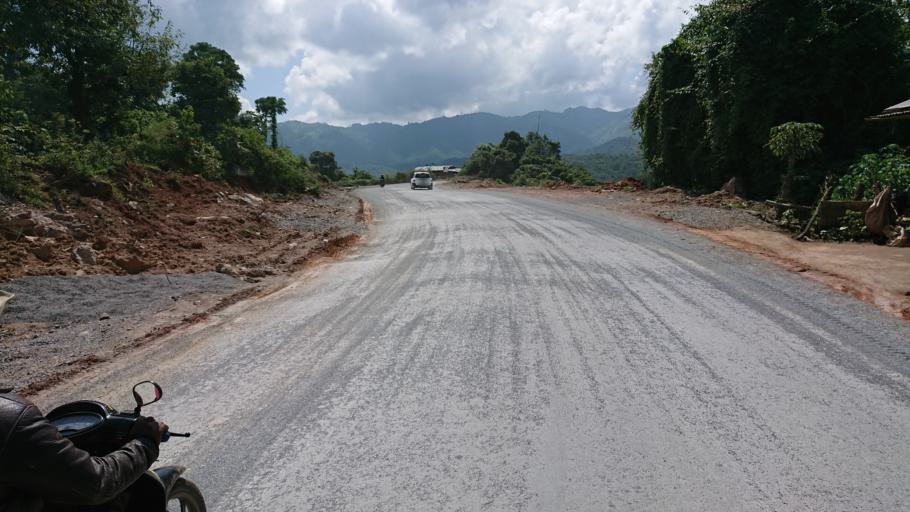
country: MM
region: Shan
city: Taunggyi
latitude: 20.8121
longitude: 97.3223
